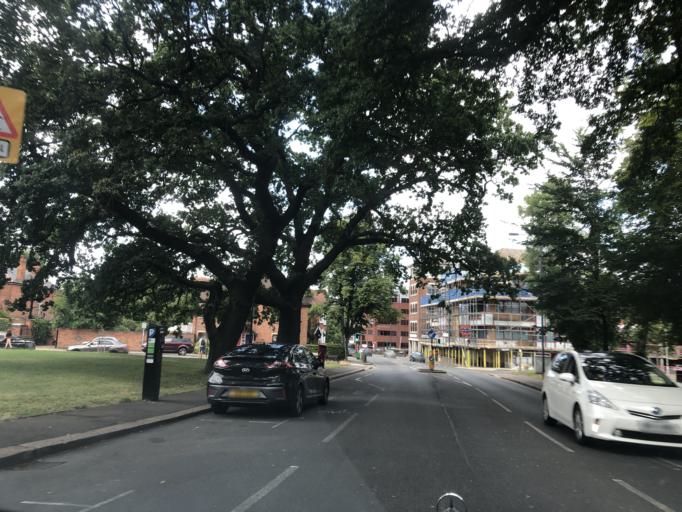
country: GB
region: England
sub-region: Greater London
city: Harrow
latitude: 51.5779
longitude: -0.3374
